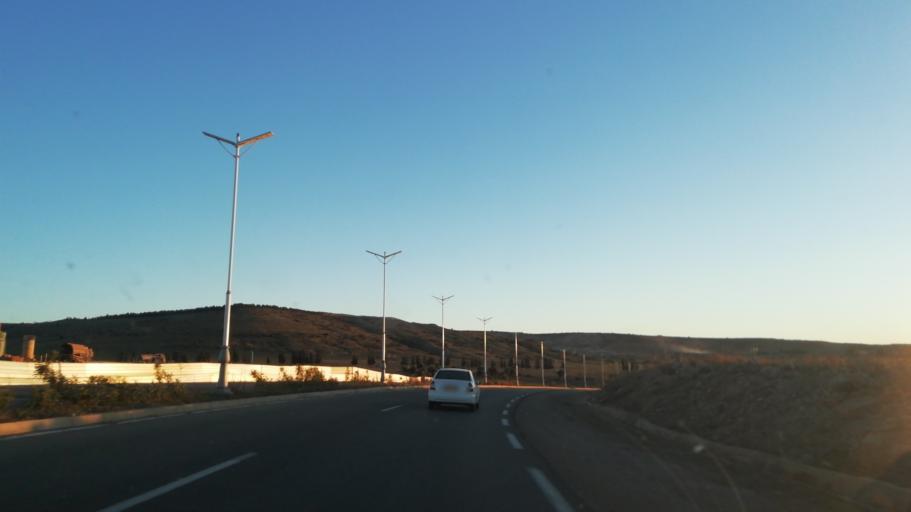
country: DZ
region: Saida
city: Saida
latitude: 34.8572
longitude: 0.1977
